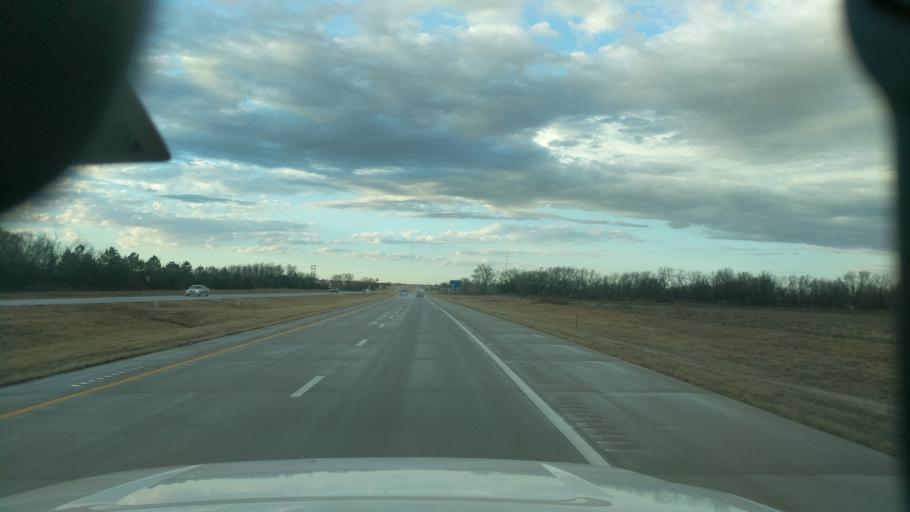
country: US
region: Kansas
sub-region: Harvey County
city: Hesston
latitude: 38.1347
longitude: -97.4050
